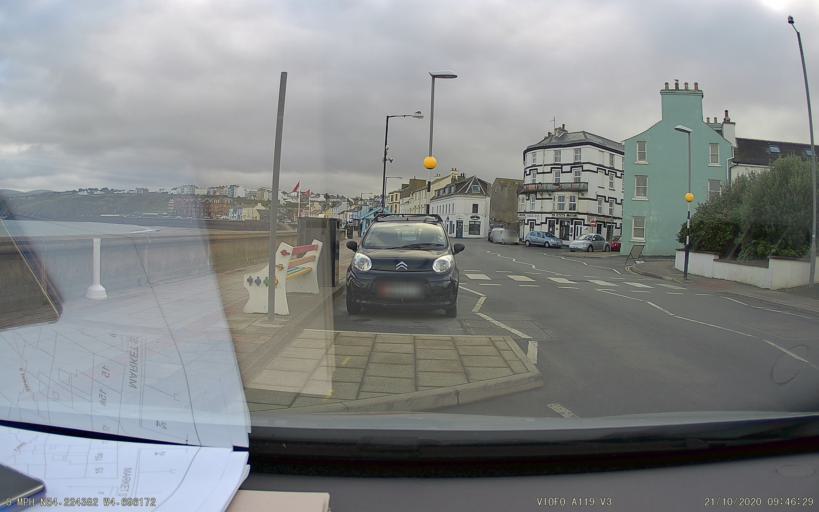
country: GB
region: England
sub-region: North Yorkshire
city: Thornton Dale
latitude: 54.2244
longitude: -0.6962
